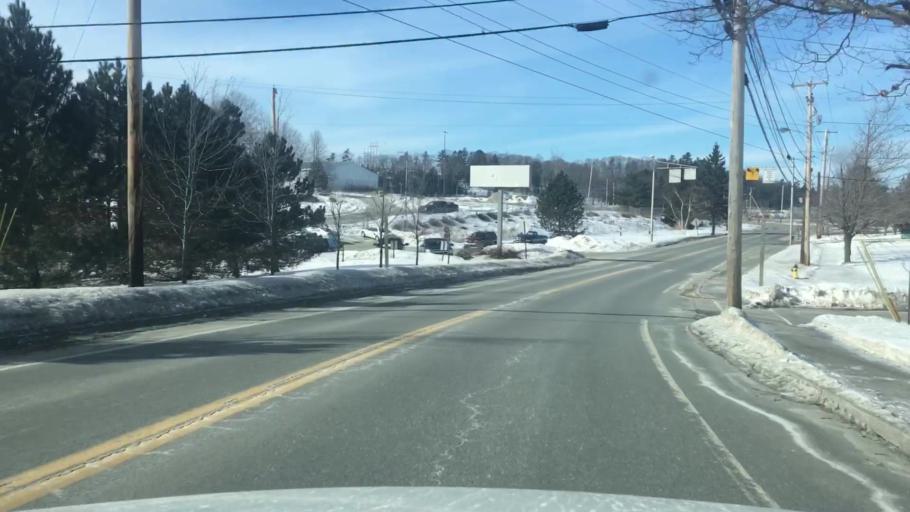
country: US
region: Maine
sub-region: Hancock County
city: Bucksport
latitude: 44.5761
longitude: -68.8030
